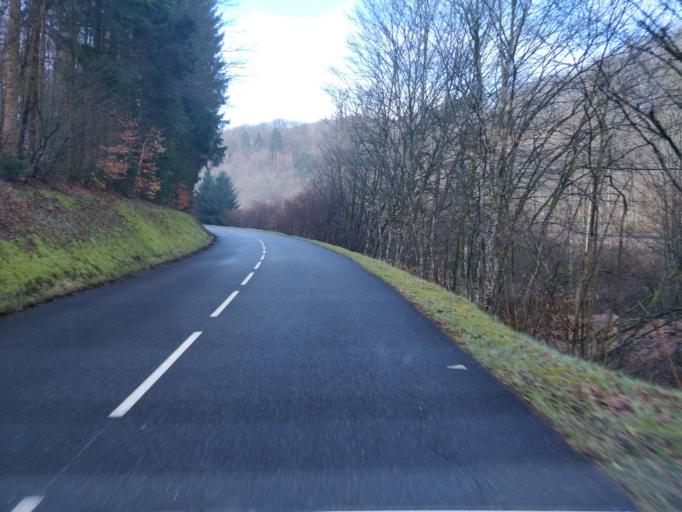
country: FR
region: Lorraine
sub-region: Departement de la Moselle
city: Soucht
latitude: 48.9228
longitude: 7.2939
